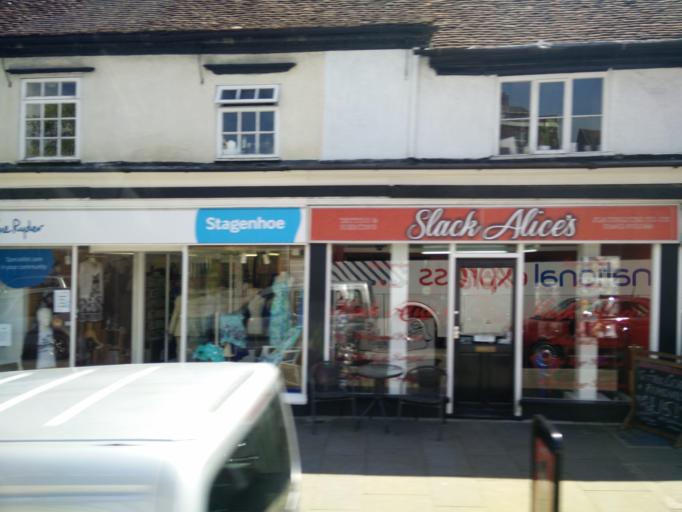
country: GB
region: England
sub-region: Hertfordshire
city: Baldock
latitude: 51.9901
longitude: -0.1882
